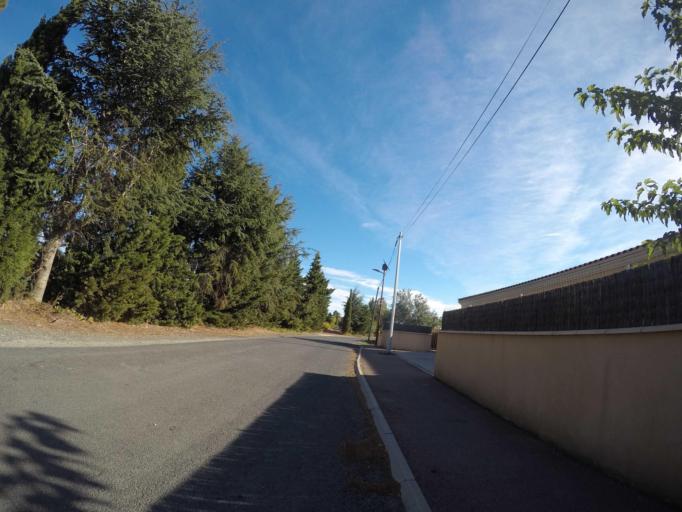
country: FR
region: Languedoc-Roussillon
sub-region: Departement des Pyrenees-Orientales
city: Villemolaque
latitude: 42.5773
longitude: 2.8084
